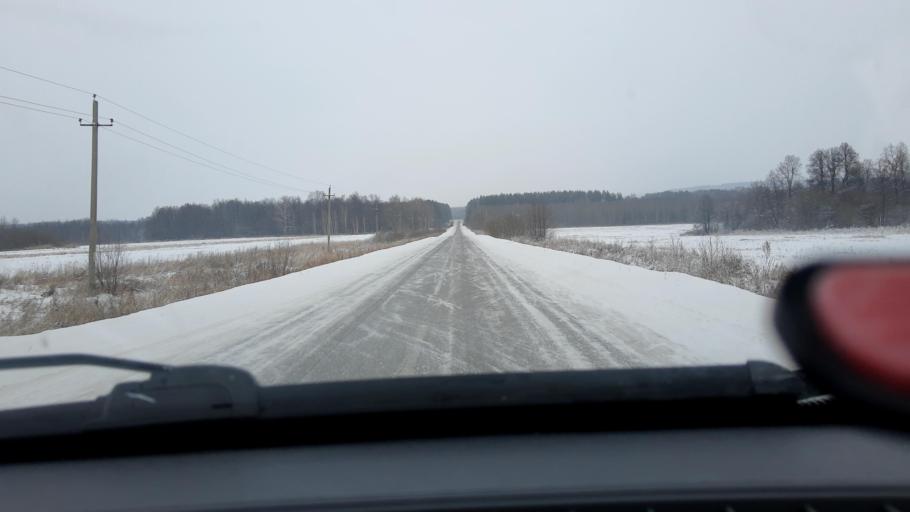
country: RU
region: Bashkortostan
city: Iglino
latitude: 54.6680
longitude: 56.4210
